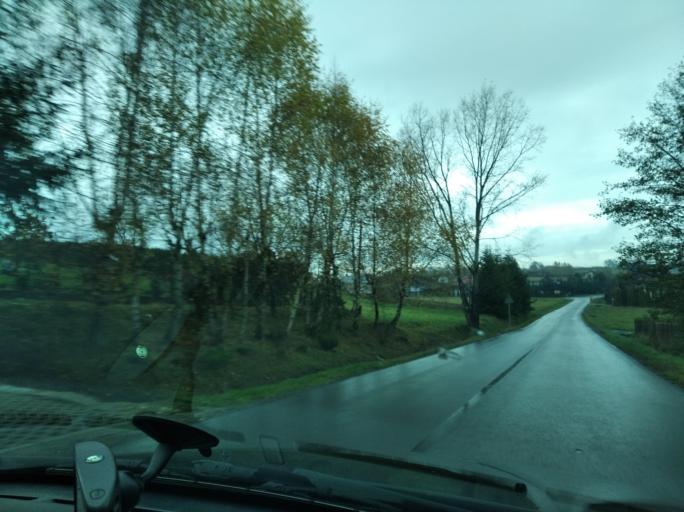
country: PL
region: Subcarpathian Voivodeship
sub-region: Powiat rzeszowski
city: Tyczyn
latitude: 49.9249
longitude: 22.0278
